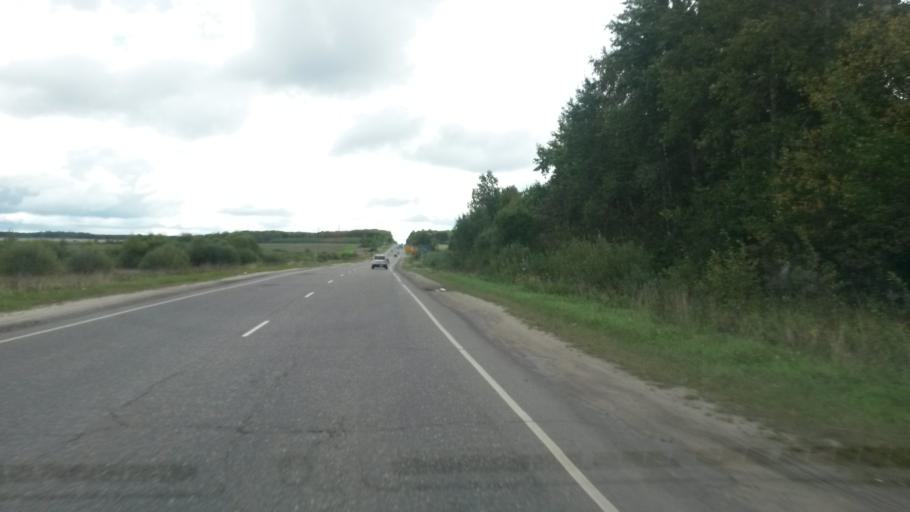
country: RU
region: Ivanovo
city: Rodniki
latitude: 57.0883
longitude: 41.6504
